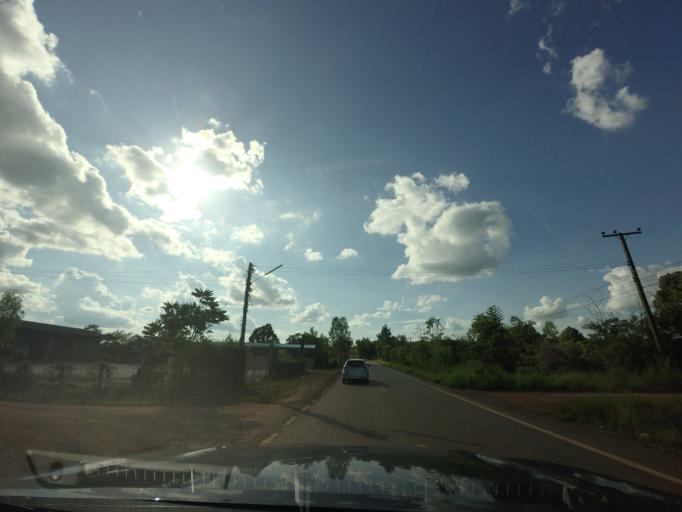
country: TH
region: Changwat Udon Thani
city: Ban Dung
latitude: 17.7435
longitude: 103.3078
